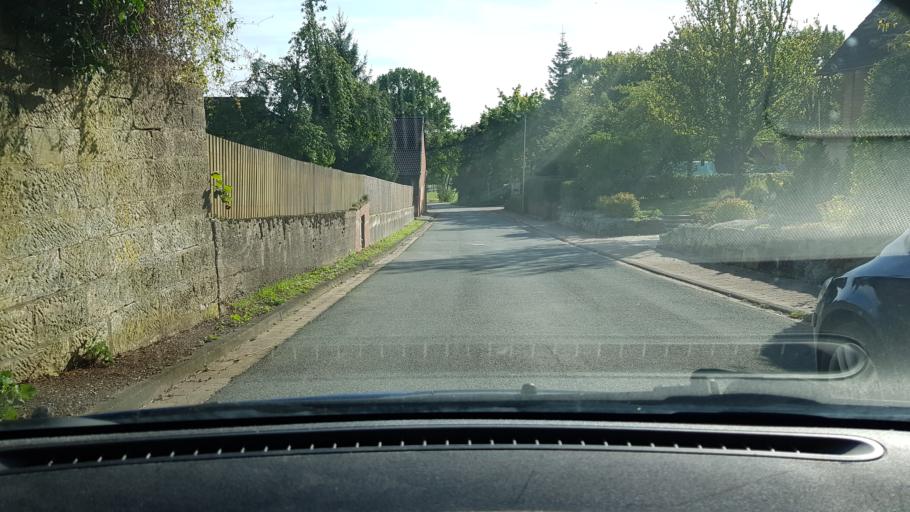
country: DE
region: Lower Saxony
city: Hameln
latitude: 52.1576
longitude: 9.3831
